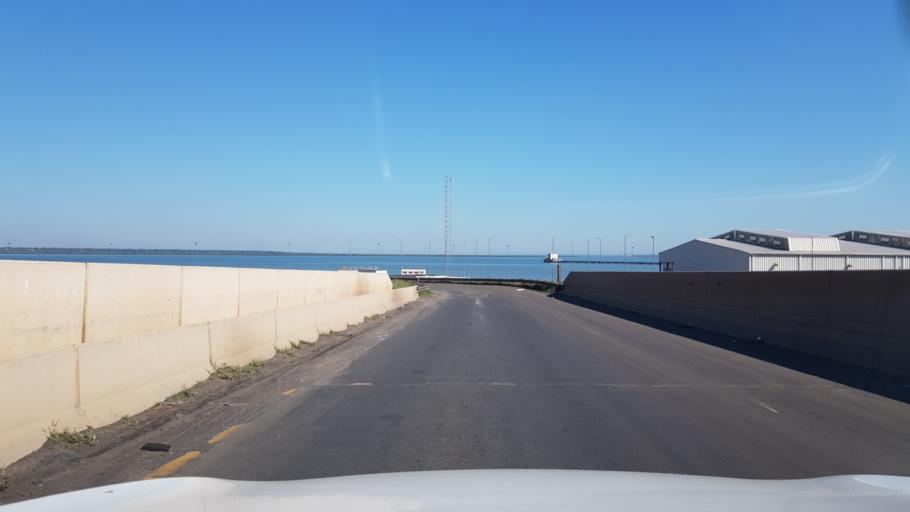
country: MZ
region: Maputo City
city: Maputo
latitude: -25.9464
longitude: 32.5380
